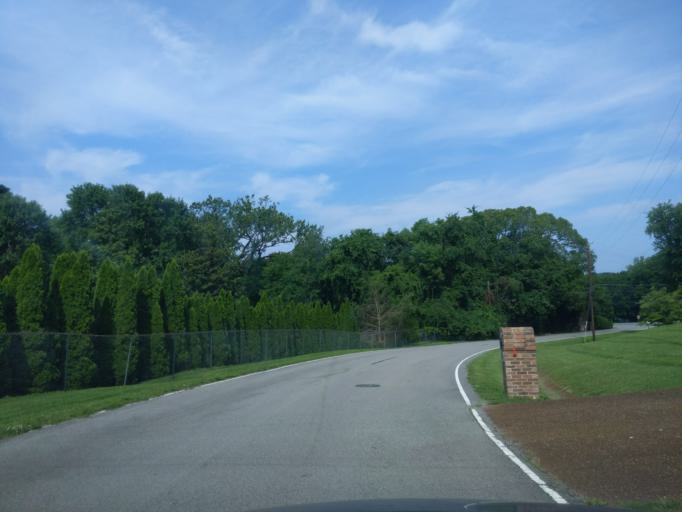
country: US
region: Tennessee
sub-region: Williamson County
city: Brentwood Estates
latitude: 36.0288
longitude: -86.7419
